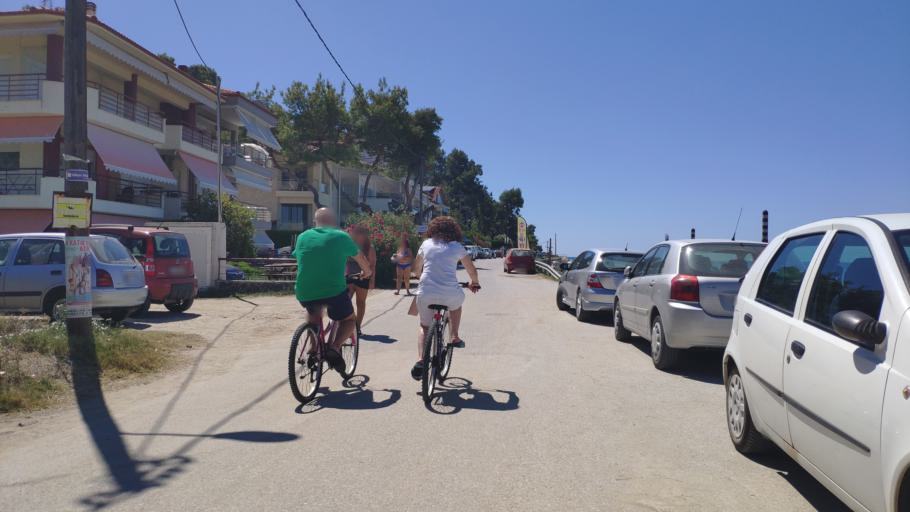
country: GR
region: Central Macedonia
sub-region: Nomos Chalkidikis
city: Kassandreia
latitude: 40.0336
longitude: 23.3602
